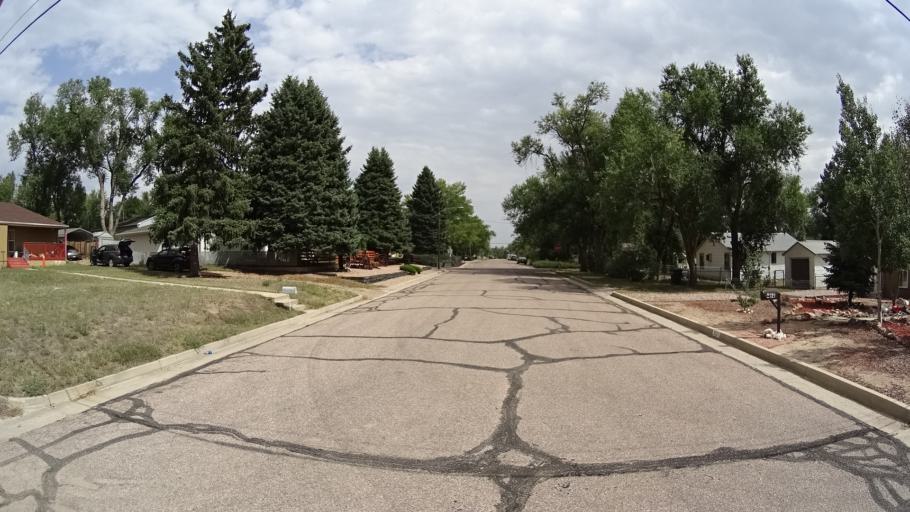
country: US
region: Colorado
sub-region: El Paso County
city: Colorado Springs
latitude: 38.8476
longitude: -104.7894
